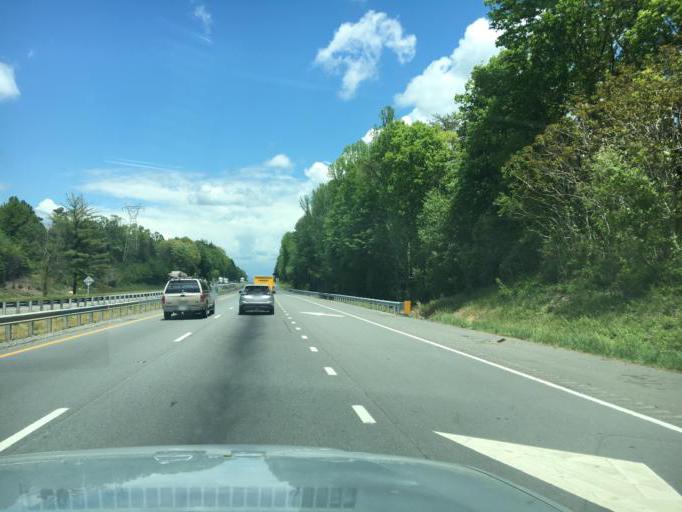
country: US
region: North Carolina
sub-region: Buncombe County
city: Weaverville
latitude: 35.6743
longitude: -82.5838
